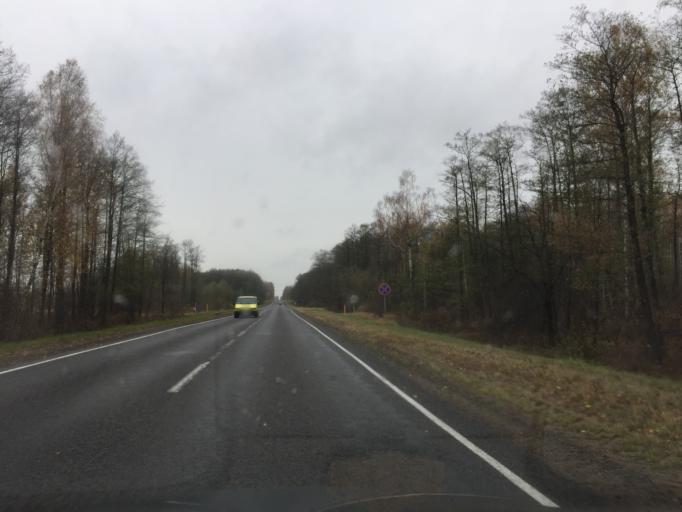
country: BY
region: Mogilev
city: Slawharad
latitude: 53.3517
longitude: 30.8241
